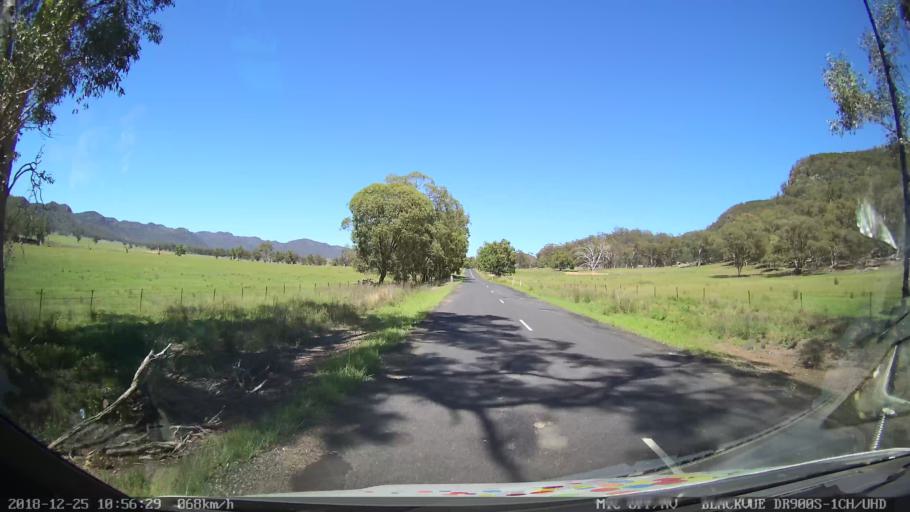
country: AU
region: New South Wales
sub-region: Upper Hunter Shire
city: Merriwa
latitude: -32.4015
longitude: 150.2622
